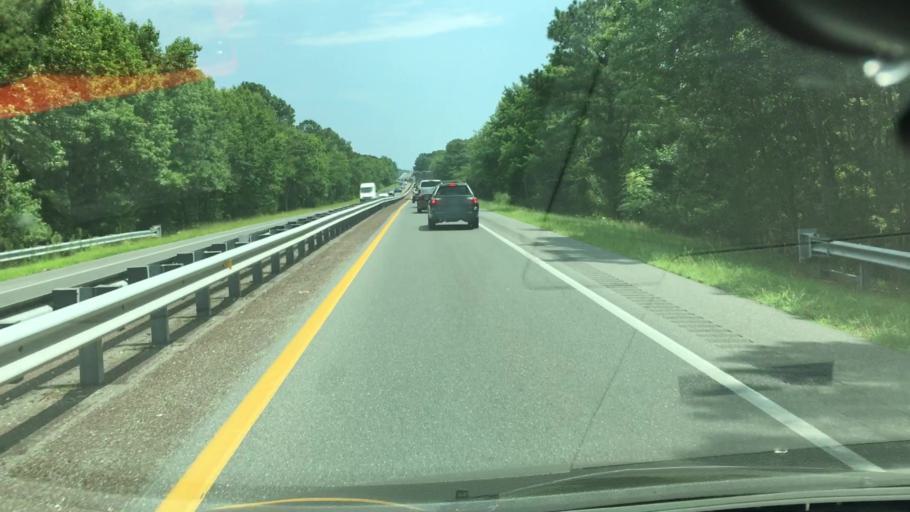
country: US
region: Maryland
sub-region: Worcester County
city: Ocean Pines
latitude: 38.3886
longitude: -75.1392
